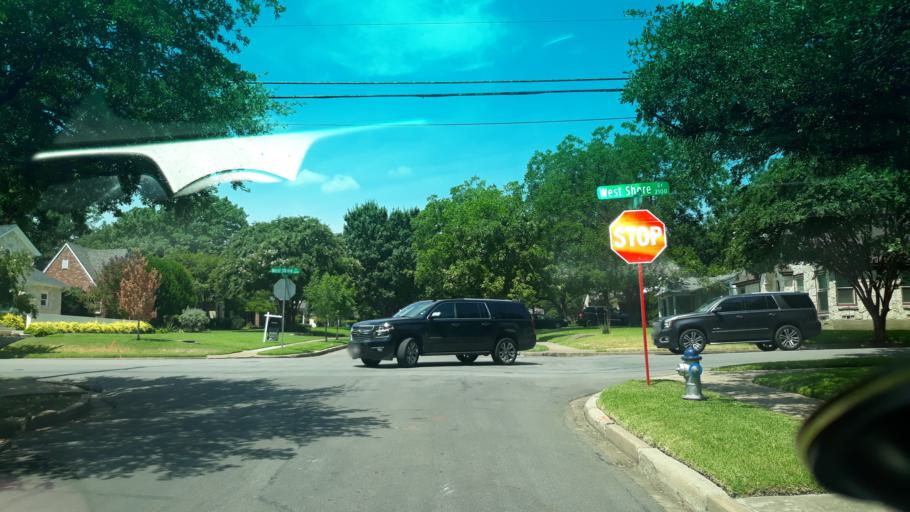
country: US
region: Texas
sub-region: Dallas County
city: Highland Park
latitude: 32.8128
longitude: -96.7379
